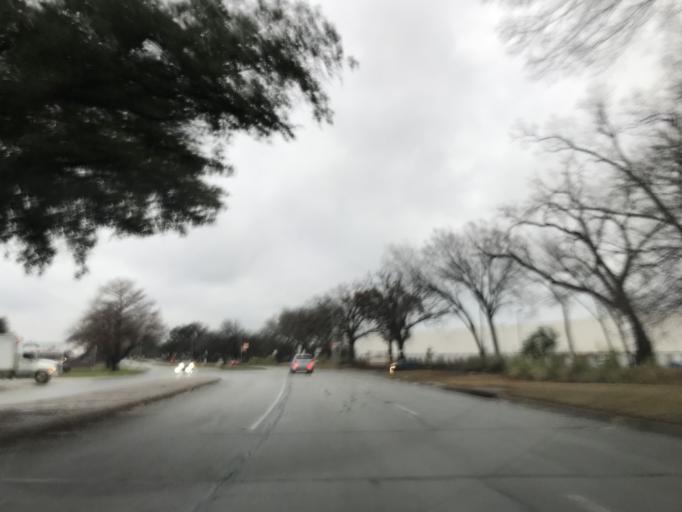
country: US
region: Texas
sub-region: Dallas County
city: Grand Prairie
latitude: 32.7719
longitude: -97.0540
